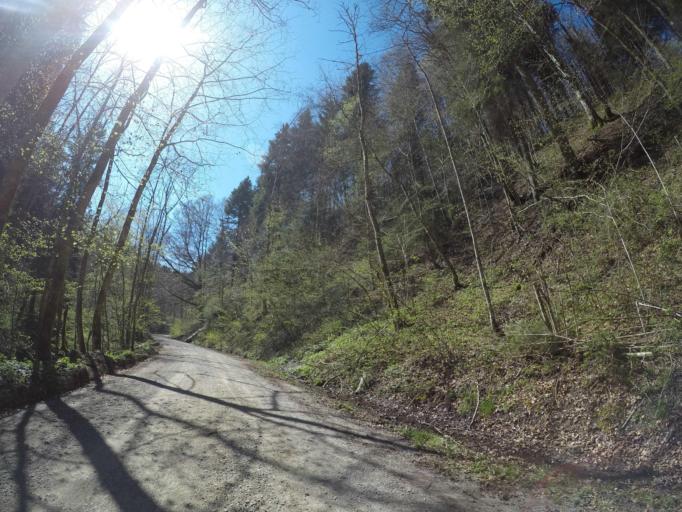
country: DE
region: Baden-Wuerttemberg
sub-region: Tuebingen Region
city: Horgenzell
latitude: 47.8051
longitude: 9.4640
